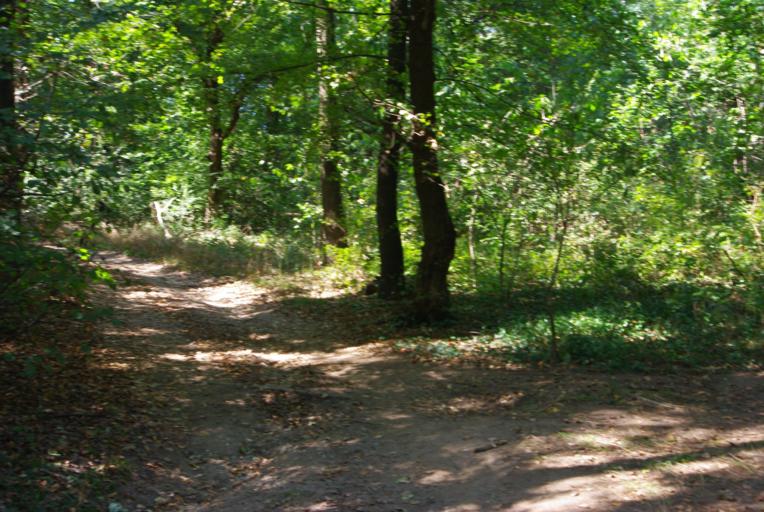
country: HU
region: Pest
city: Toeroekbalint
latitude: 47.4273
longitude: 18.9200
